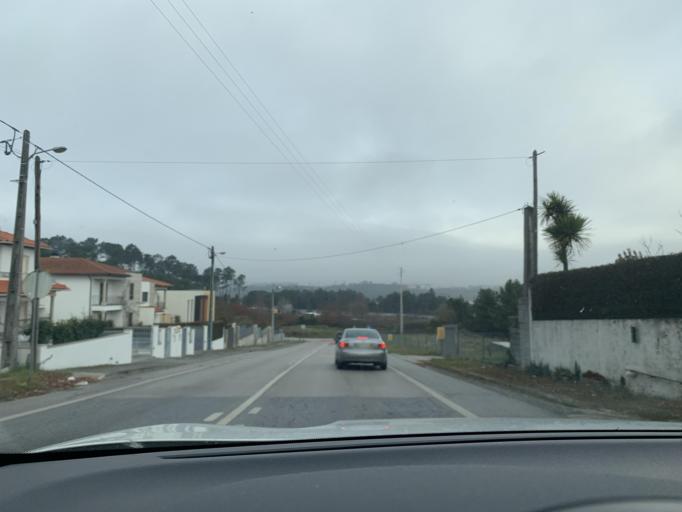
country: PT
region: Viseu
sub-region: Viseu
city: Viseu
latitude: 40.6259
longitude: -7.8999
